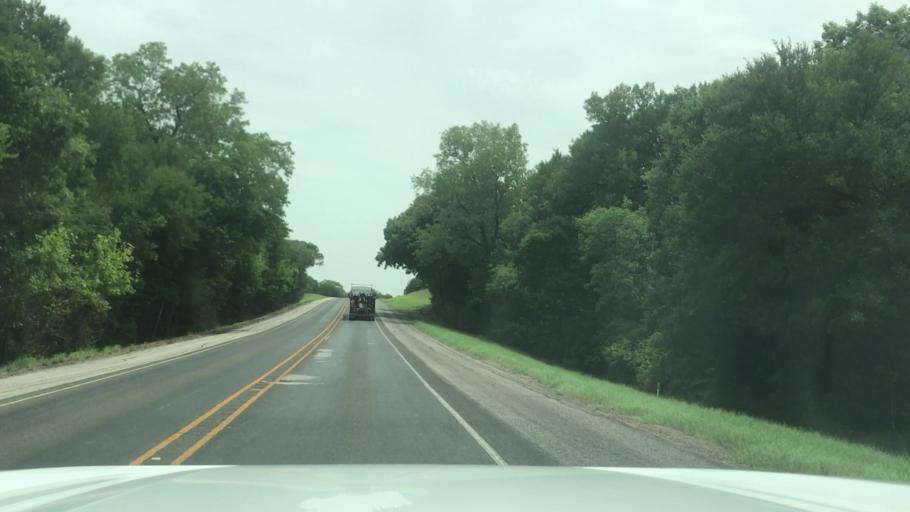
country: US
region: Texas
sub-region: Bosque County
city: Meridian
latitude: 31.8992
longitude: -97.6539
